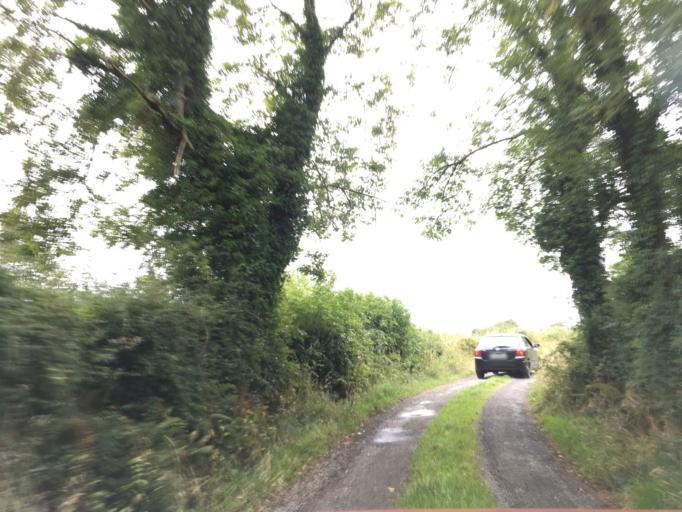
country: IE
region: Munster
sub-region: An Clar
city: Ennis
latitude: 52.7240
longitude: -9.0945
